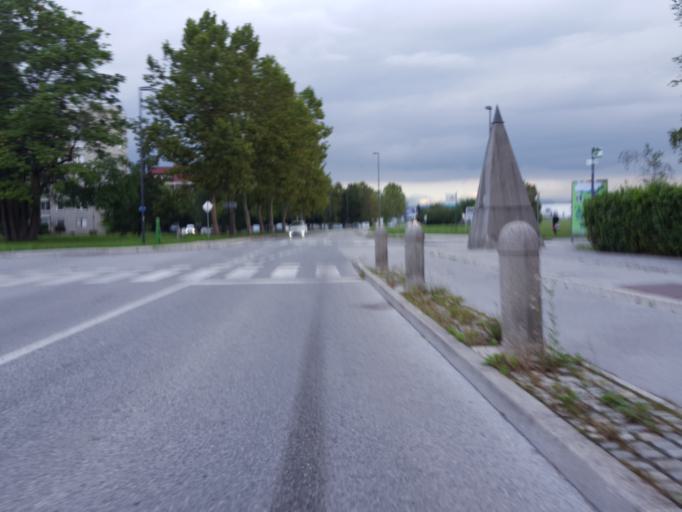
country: SI
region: Skofljica
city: Lavrica
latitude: 46.0503
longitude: 14.5649
